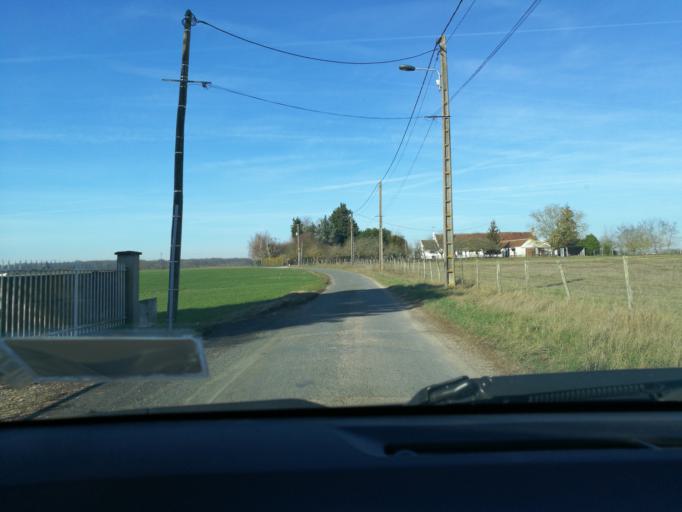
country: FR
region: Centre
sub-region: Departement du Loiret
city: Chaingy
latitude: 47.8886
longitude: 1.7617
